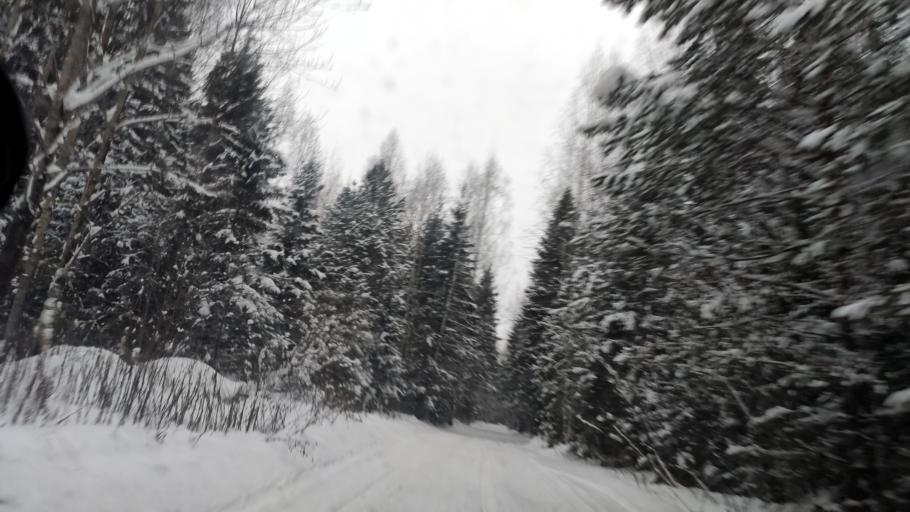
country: RU
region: Perm
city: Krasnokamsk
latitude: 57.9945
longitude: 55.7825
